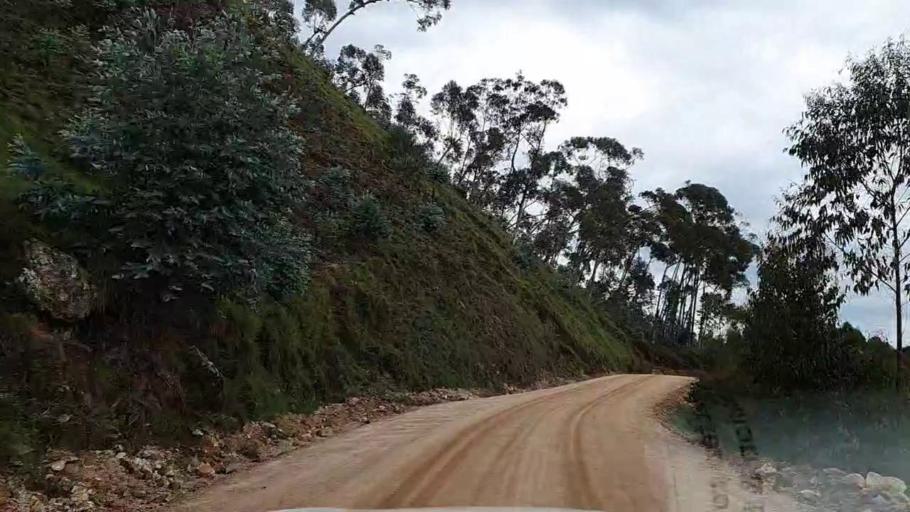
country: RW
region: Southern Province
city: Nzega
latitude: -2.3759
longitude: 29.4492
